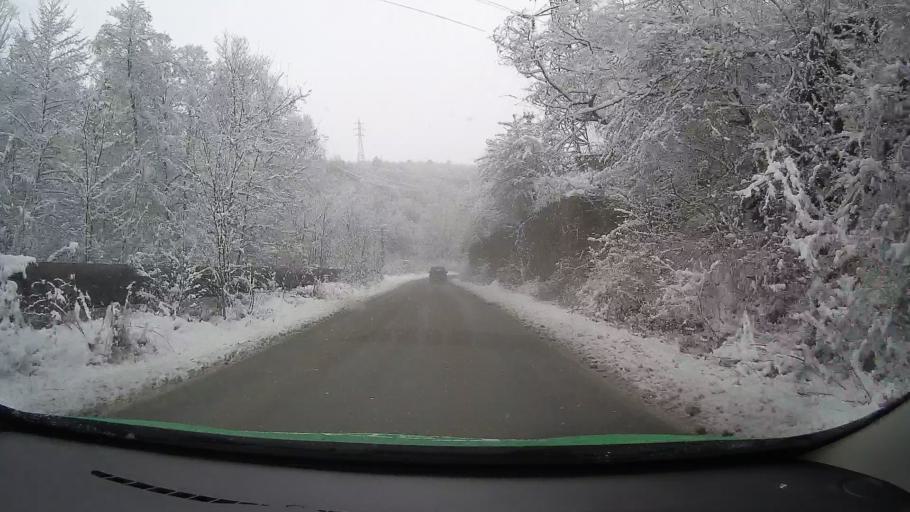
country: RO
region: Hunedoara
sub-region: Comuna Teliucu Inferior
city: Teliucu Inferior
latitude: 45.7308
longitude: 22.8815
